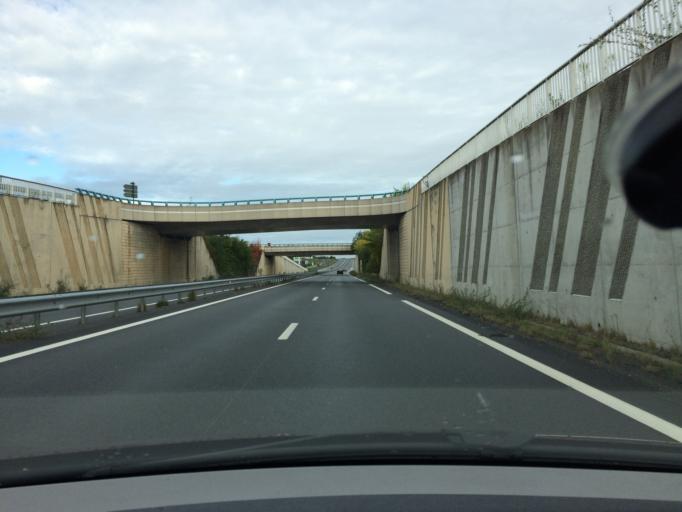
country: FR
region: Brittany
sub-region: Departement d'Ille-et-Vilaine
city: Janze
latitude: 47.9699
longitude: -1.5351
